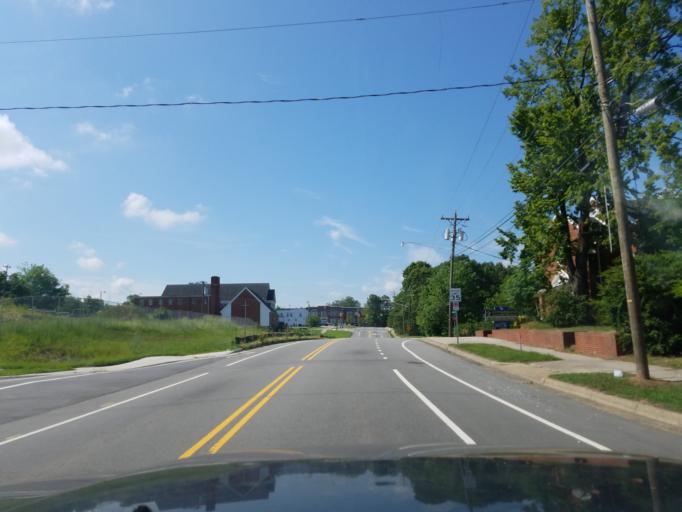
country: US
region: North Carolina
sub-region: Durham County
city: Durham
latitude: 35.9853
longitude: -78.9027
